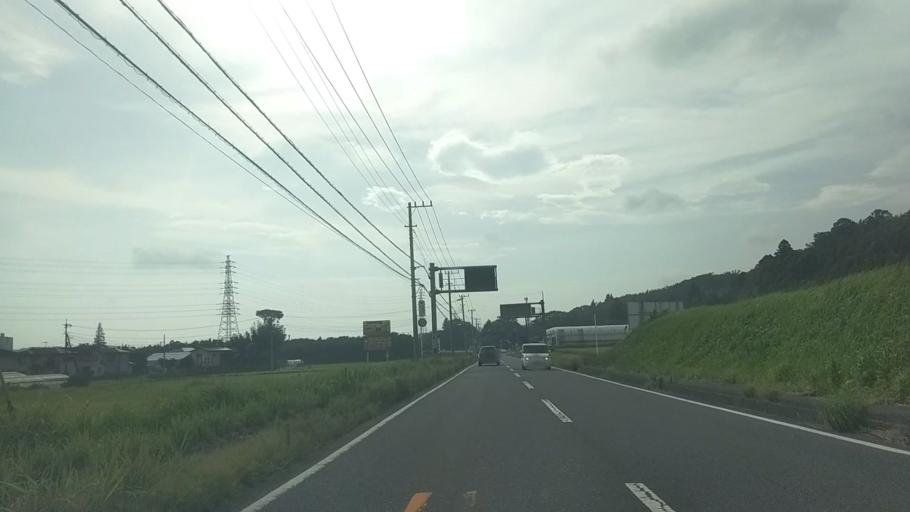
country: JP
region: Chiba
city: Kimitsu
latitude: 35.3106
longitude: 139.9667
